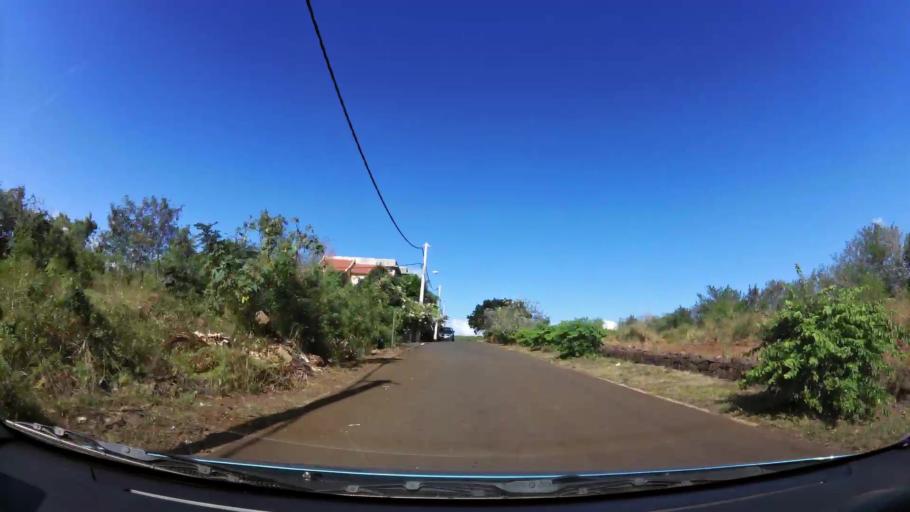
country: MU
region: Black River
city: Albion
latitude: -20.2202
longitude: 57.4031
